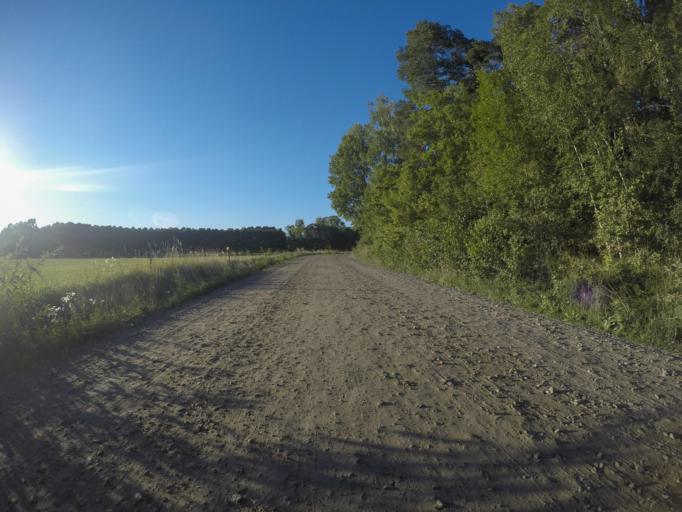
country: SE
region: Vaestmanland
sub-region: Vasteras
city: Vasteras
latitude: 59.5532
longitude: 16.6643
